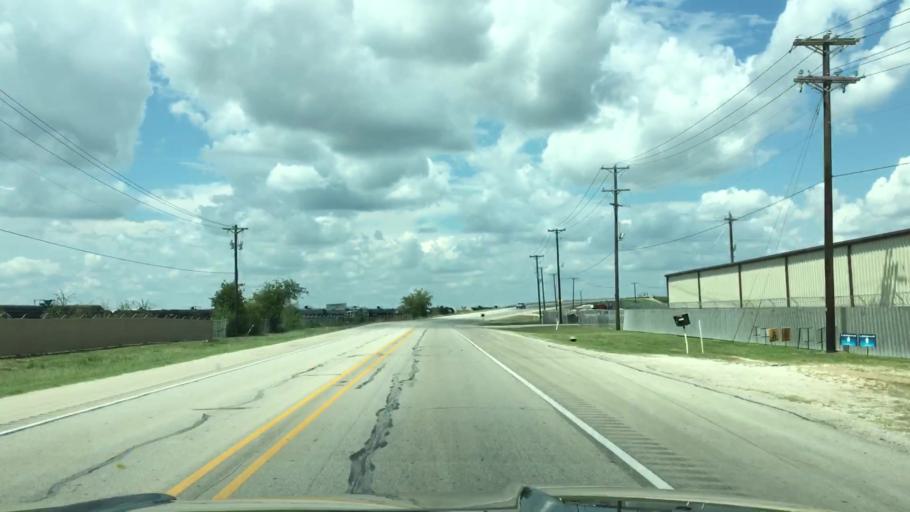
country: US
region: Texas
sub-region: Tarrant County
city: Eagle Mountain
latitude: 32.9395
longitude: -97.4200
